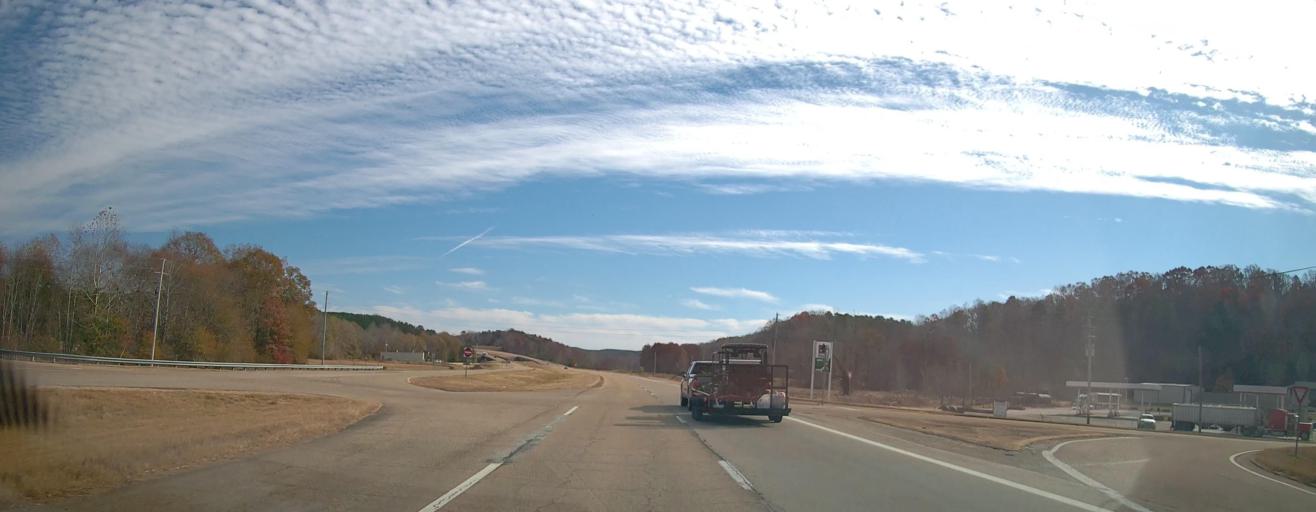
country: US
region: Mississippi
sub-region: Alcorn County
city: Corinth
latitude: 34.9363
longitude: -88.7746
